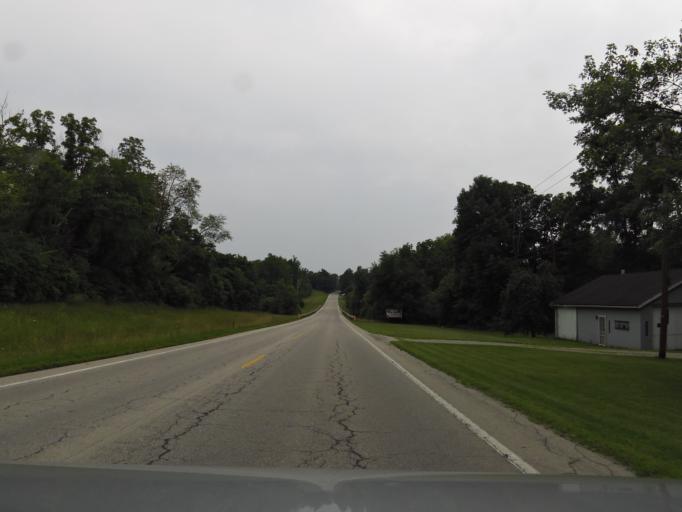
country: US
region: Ohio
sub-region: Clinton County
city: Wilmington
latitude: 39.3856
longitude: -83.8598
